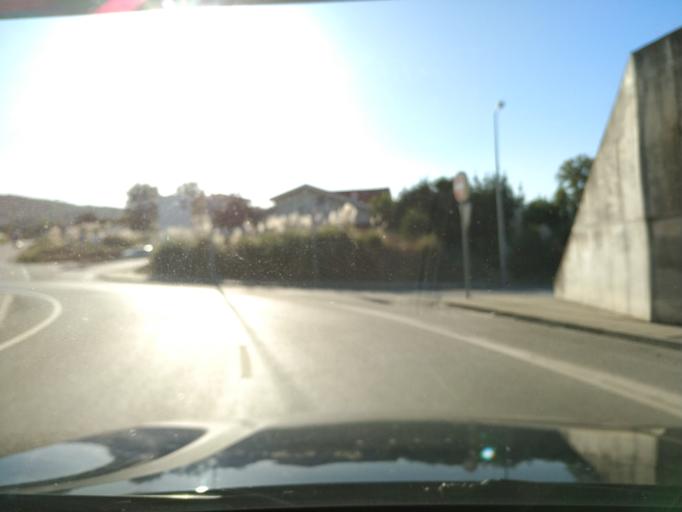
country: PT
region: Porto
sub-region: Vila Nova de Gaia
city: Canelas
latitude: 41.0882
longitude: -8.6040
